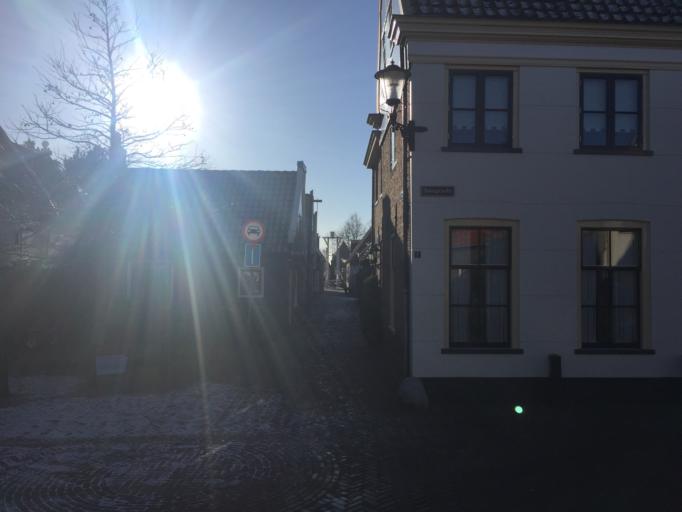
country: NL
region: North Holland
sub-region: Gemeente Beemster
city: Halfweg
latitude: 52.5595
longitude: 4.8546
